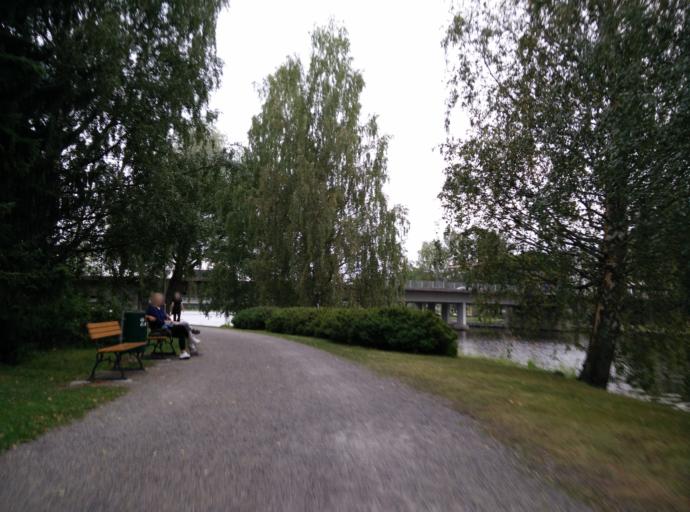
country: FI
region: Haeme
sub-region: Haemeenlinna
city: Haemeenlinna
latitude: 60.9986
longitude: 24.4730
